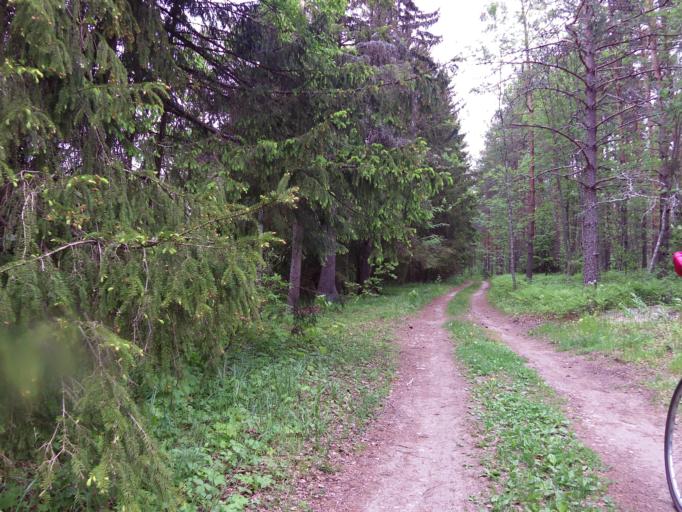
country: EE
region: Harju
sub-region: Paldiski linn
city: Paldiski
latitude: 59.2514
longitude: 23.7497
